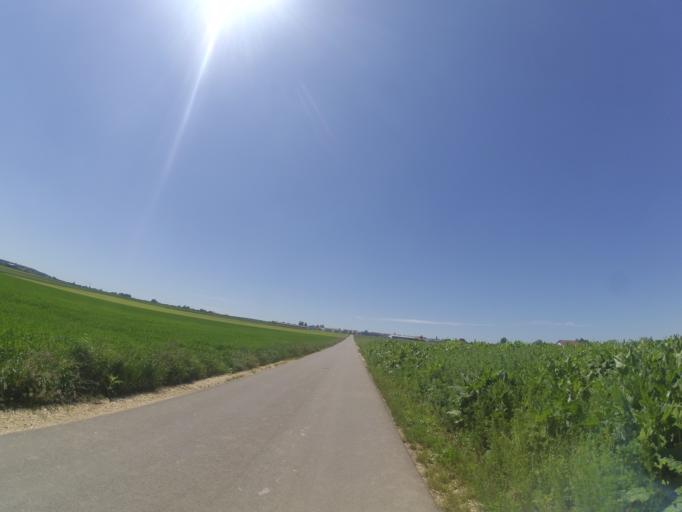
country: DE
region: Baden-Wuerttemberg
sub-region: Tuebingen Region
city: Blaubeuren
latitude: 48.4687
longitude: 9.8495
